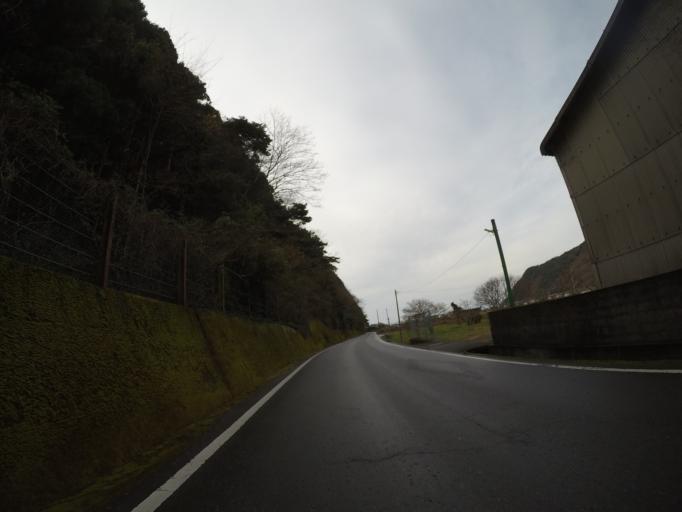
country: JP
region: Shizuoka
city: Heda
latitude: 34.8468
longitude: 138.7838
